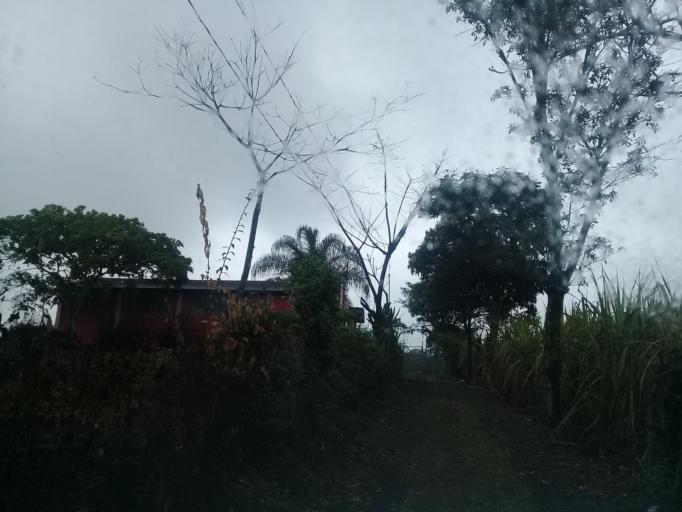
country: MX
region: Veracruz
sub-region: Amatlan de los Reyes
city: Centro de Readaptacion Social
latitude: 18.8206
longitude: -96.9451
